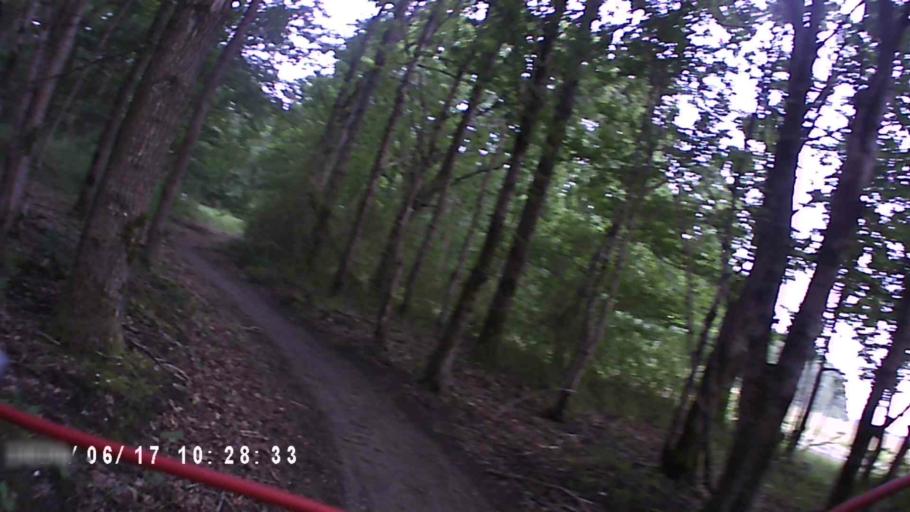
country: NL
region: Groningen
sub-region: Gemeente De Marne
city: Ulrum
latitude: 53.3959
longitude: 6.2415
